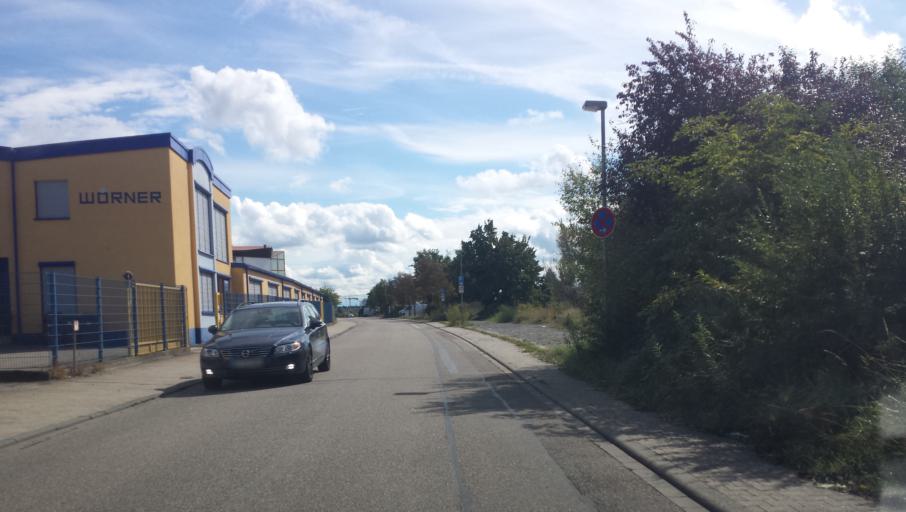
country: DE
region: Baden-Wuerttemberg
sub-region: Karlsruhe Region
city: Altlussheim
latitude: 49.2911
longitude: 8.5059
